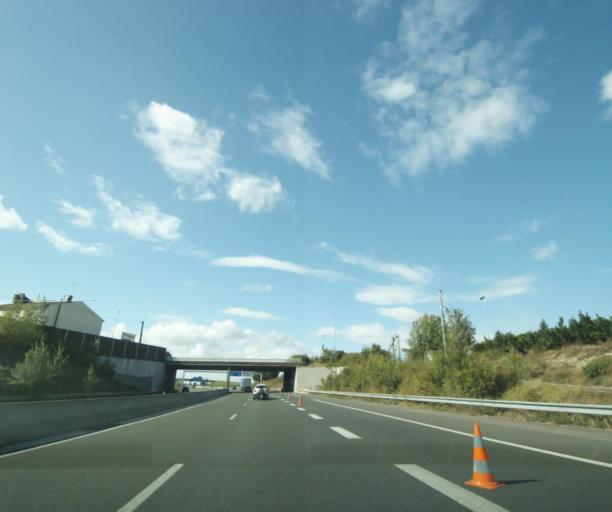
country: FR
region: Centre
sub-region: Departement du Loiret
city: Saint-Pryve-Saint-Mesmin
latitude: 47.8939
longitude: 1.8544
